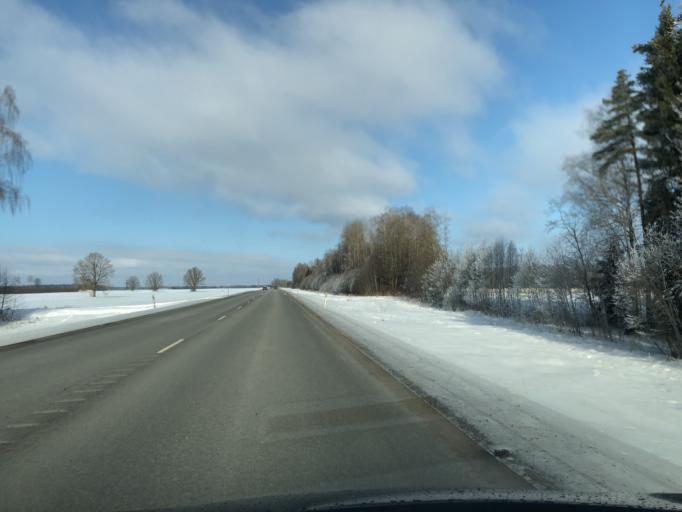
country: EE
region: Jogevamaa
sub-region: Poltsamaa linn
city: Poltsamaa
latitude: 58.7598
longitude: 25.7620
